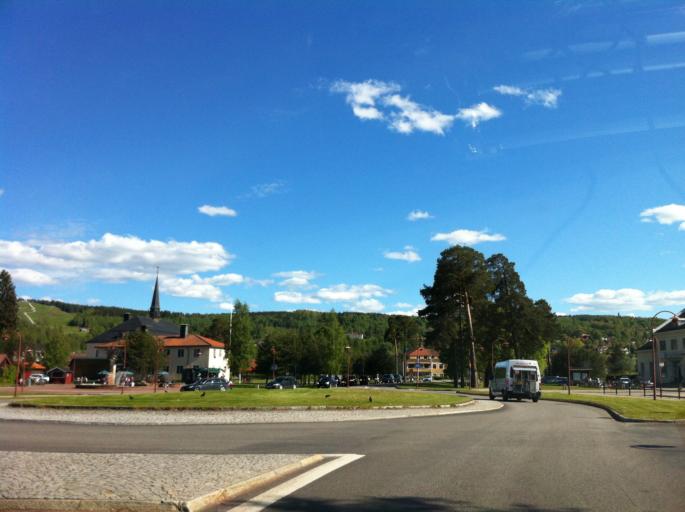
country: SE
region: Dalarna
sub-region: Rattviks Kommun
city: Raettvik
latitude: 60.8859
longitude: 15.1159
